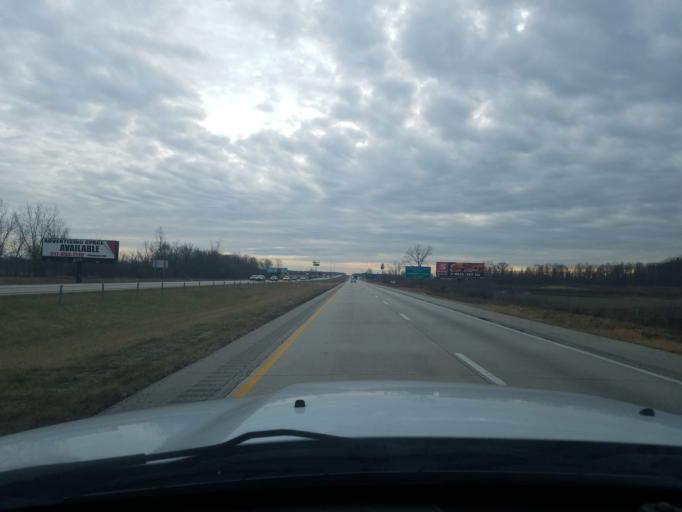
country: US
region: Indiana
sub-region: Grant County
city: Gas City
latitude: 40.5649
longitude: -85.5513
